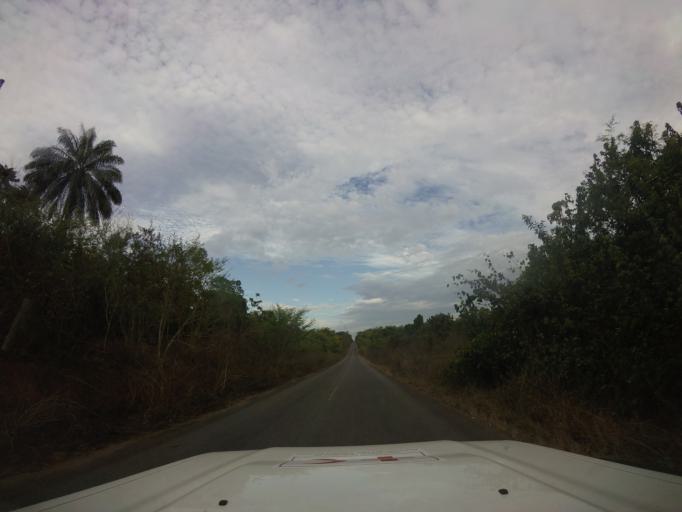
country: LR
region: Bomi
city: Tubmanburg
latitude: 6.6956
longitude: -10.9024
